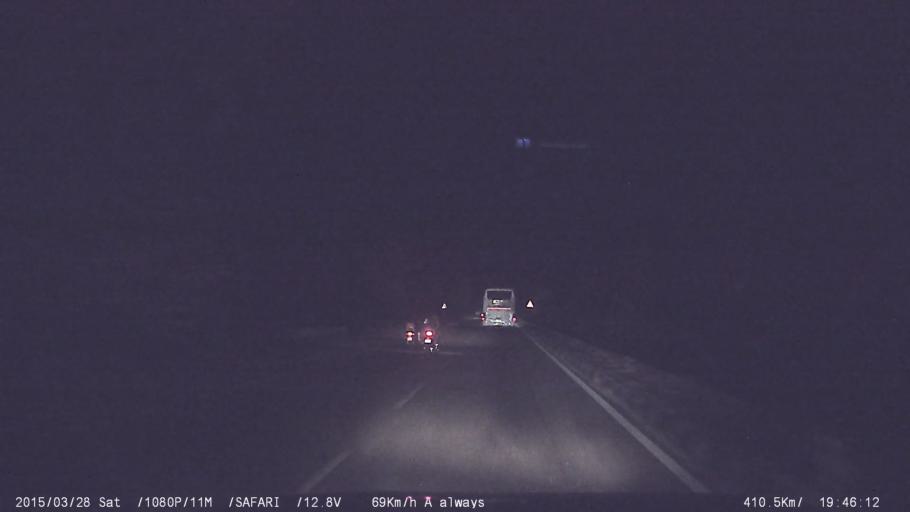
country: IN
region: Karnataka
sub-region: Mandya
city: Pandavapura
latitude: 12.4844
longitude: 76.7774
